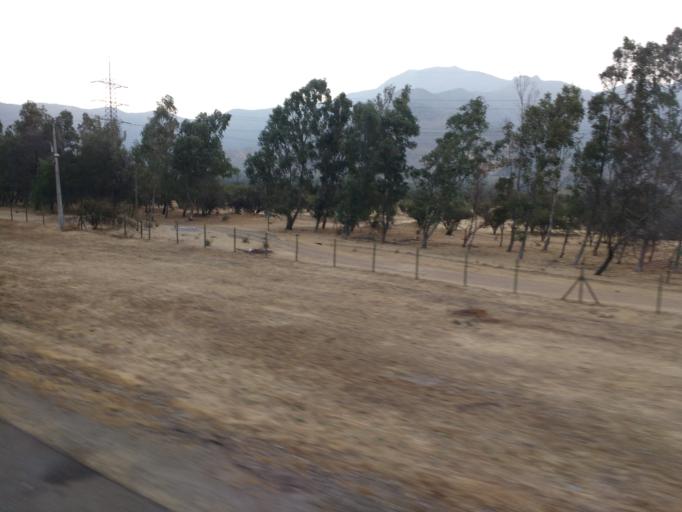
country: CL
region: Santiago Metropolitan
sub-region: Provincia de Talagante
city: Penaflor
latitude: -33.4575
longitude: -70.9029
